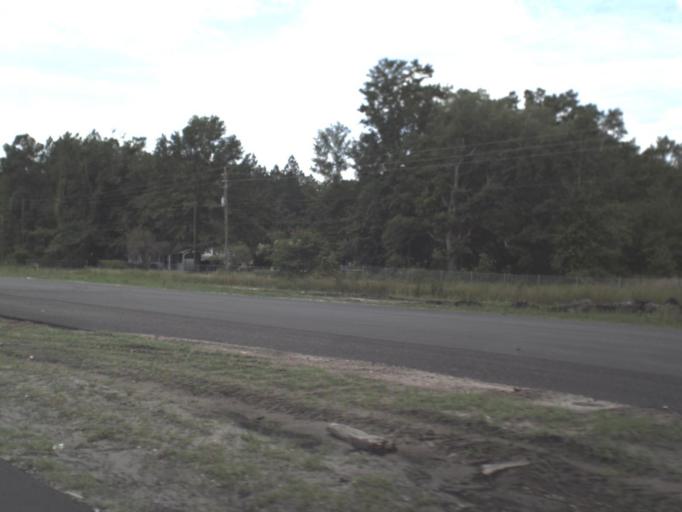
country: US
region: Florida
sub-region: Nassau County
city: Nassau Village-Ratliff
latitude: 30.4328
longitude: -81.9224
